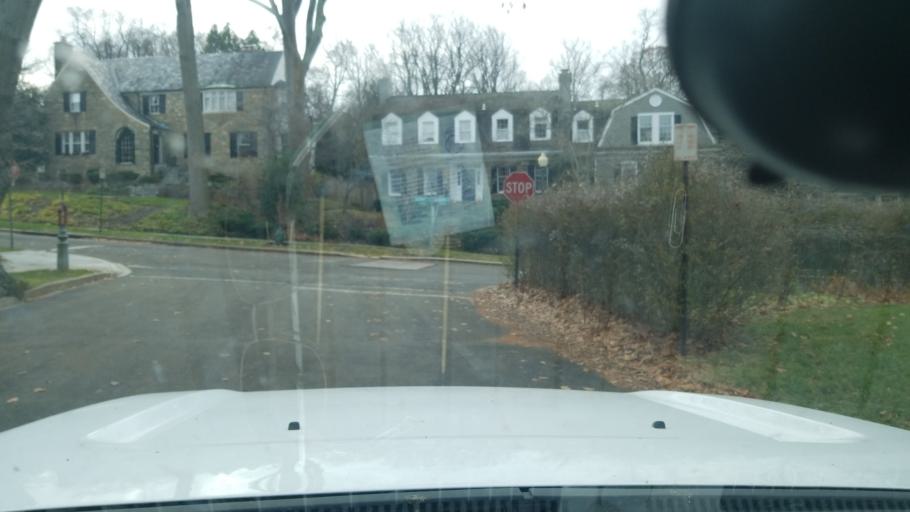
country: US
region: Maryland
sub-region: Montgomery County
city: Friendship Village
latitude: 38.9384
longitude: -77.0944
